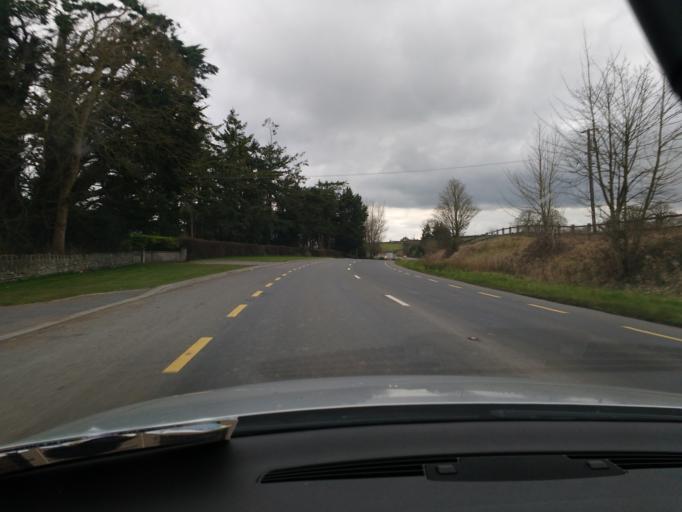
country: IE
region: Leinster
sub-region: Kilkenny
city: Kilkenny
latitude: 52.6820
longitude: -7.2745
